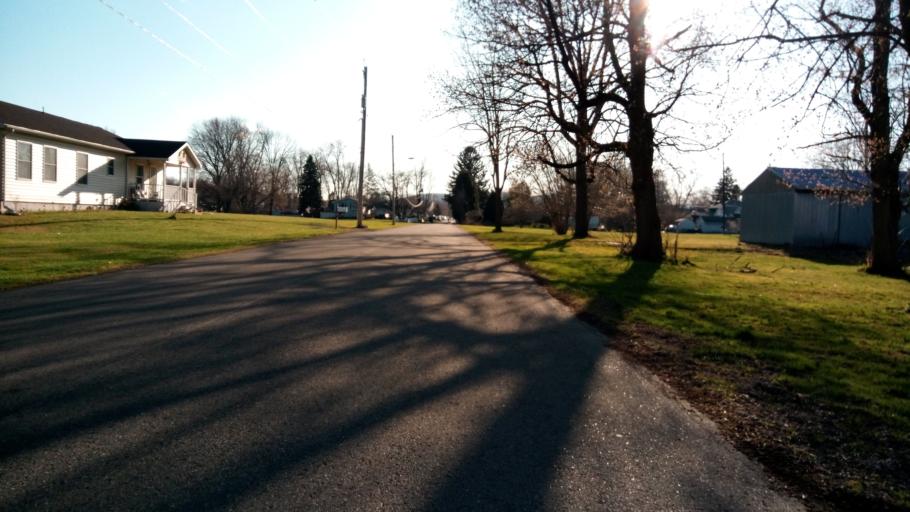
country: US
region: New York
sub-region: Chemung County
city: Elmira
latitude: 42.0776
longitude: -76.7802
